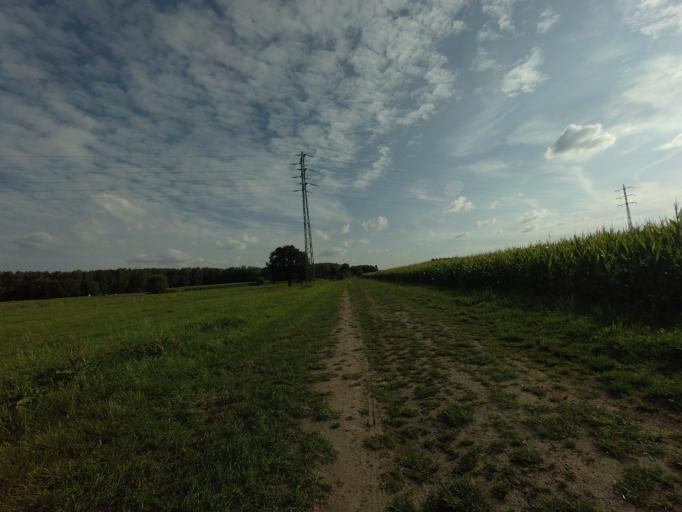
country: BE
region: Flanders
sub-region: Provincie Vlaams-Brabant
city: Kapelle-op-den-Bos
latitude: 51.0248
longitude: 4.3425
